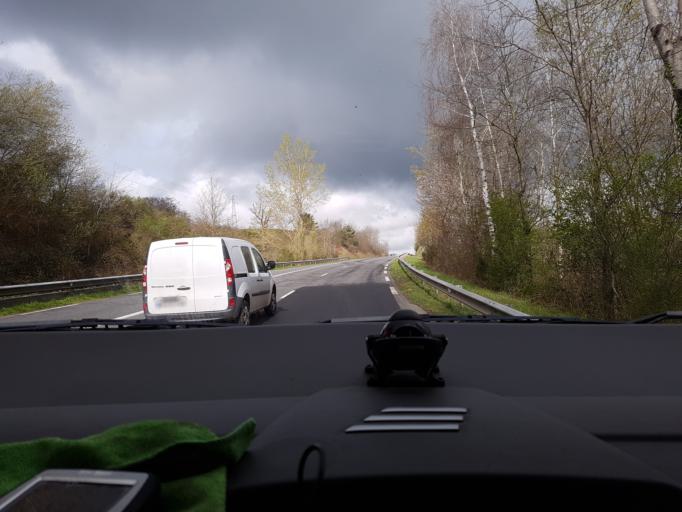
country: FR
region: Midi-Pyrenees
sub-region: Departement de l'Aveyron
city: Moyrazes
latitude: 44.3792
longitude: 2.4135
